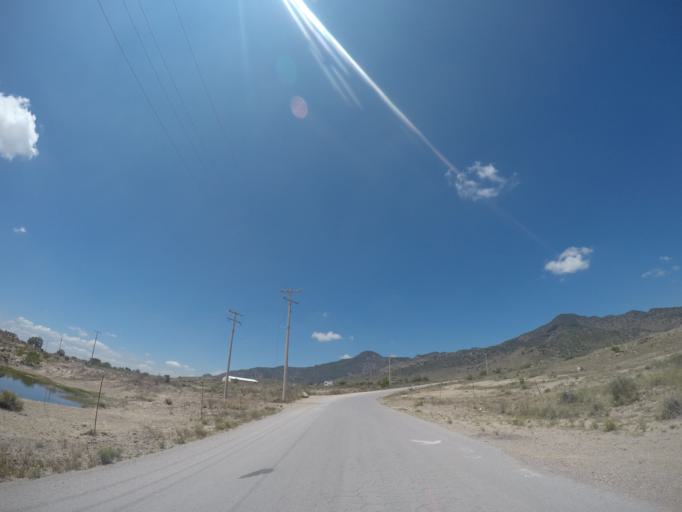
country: MX
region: San Luis Potosi
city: La Pila
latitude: 22.0147
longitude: -100.9114
